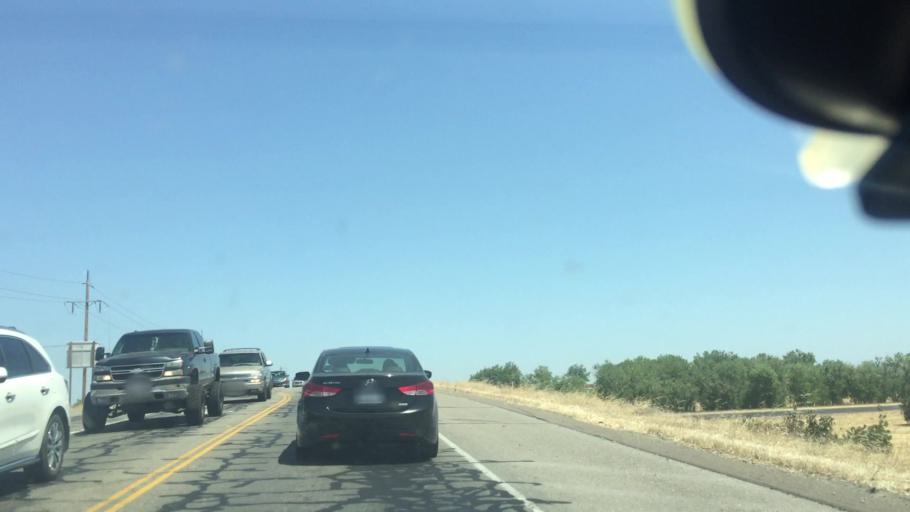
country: US
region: California
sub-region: San Joaquin County
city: Manteca
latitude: 37.7819
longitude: -121.2521
